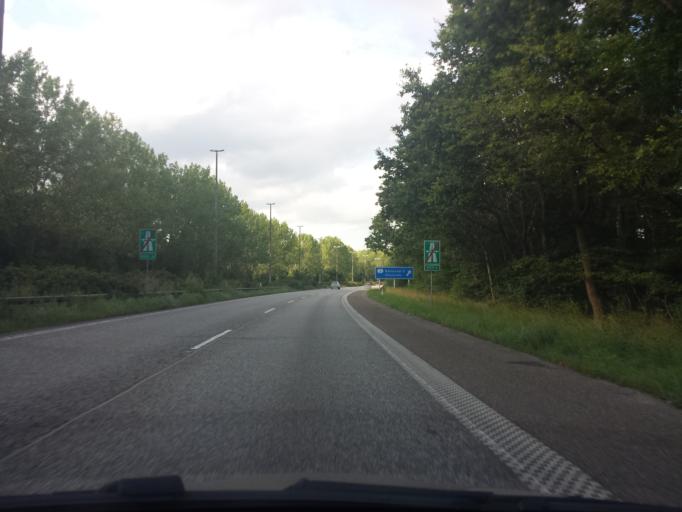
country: DK
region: Capital Region
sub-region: Ballerup Kommune
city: Ballerup
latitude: 55.7179
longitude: 12.3653
